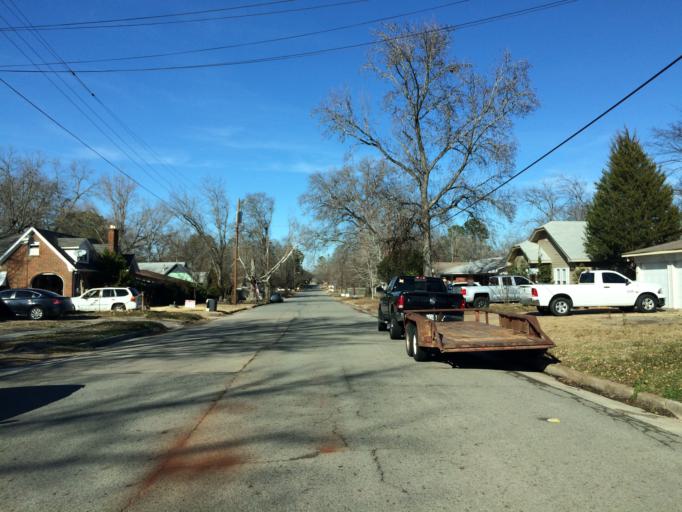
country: US
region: Texas
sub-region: Wood County
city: Mineola
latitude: 32.6685
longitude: -95.4853
